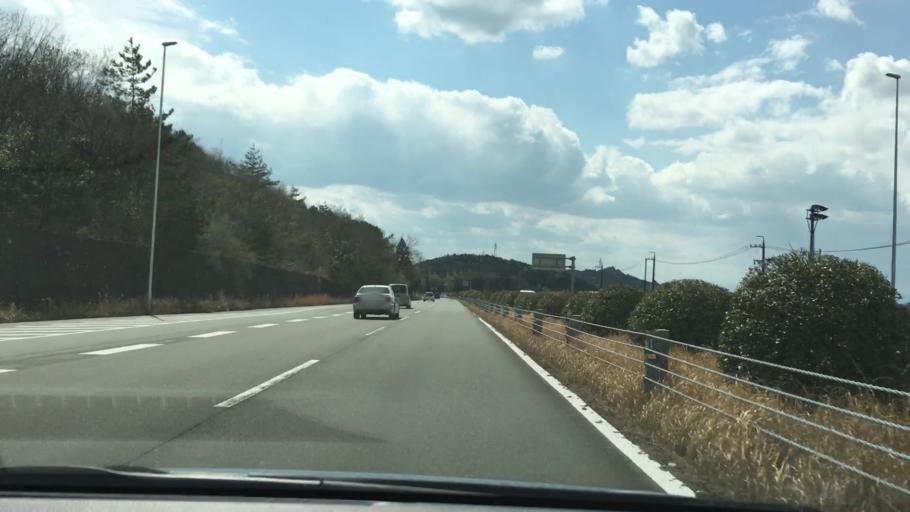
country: JP
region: Mie
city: Ise
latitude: 34.4907
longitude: 136.7643
